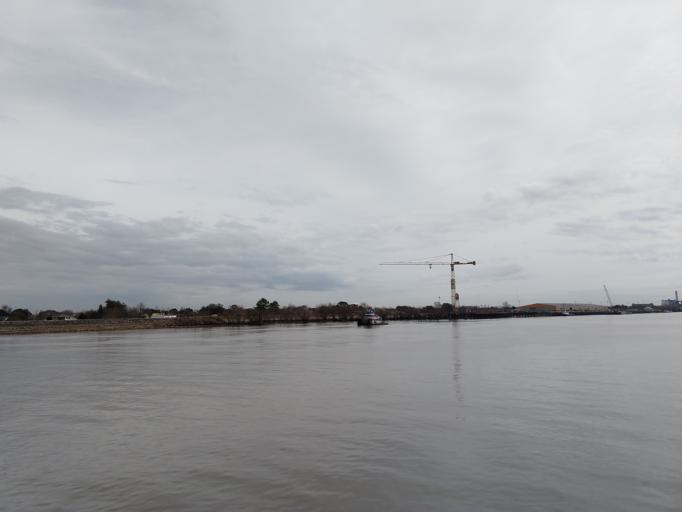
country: US
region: Louisiana
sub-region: Saint Bernard Parish
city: Arabi
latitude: 29.9544
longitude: -90.0270
